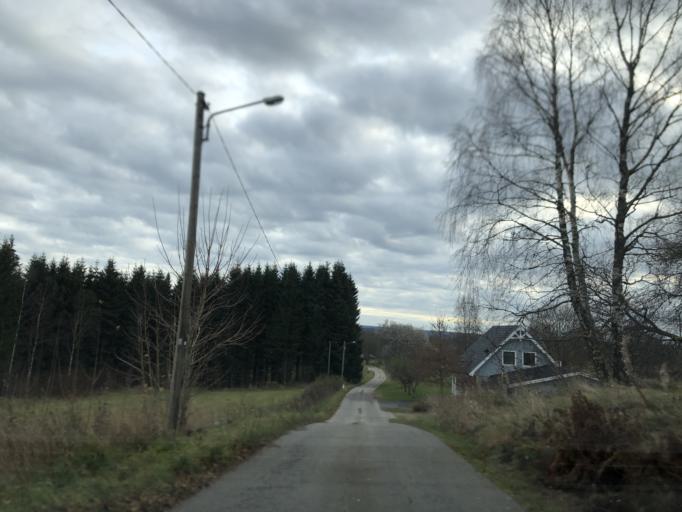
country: SE
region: Vaestra Goetaland
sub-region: Ulricehamns Kommun
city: Ulricehamn
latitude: 57.7291
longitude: 13.3183
